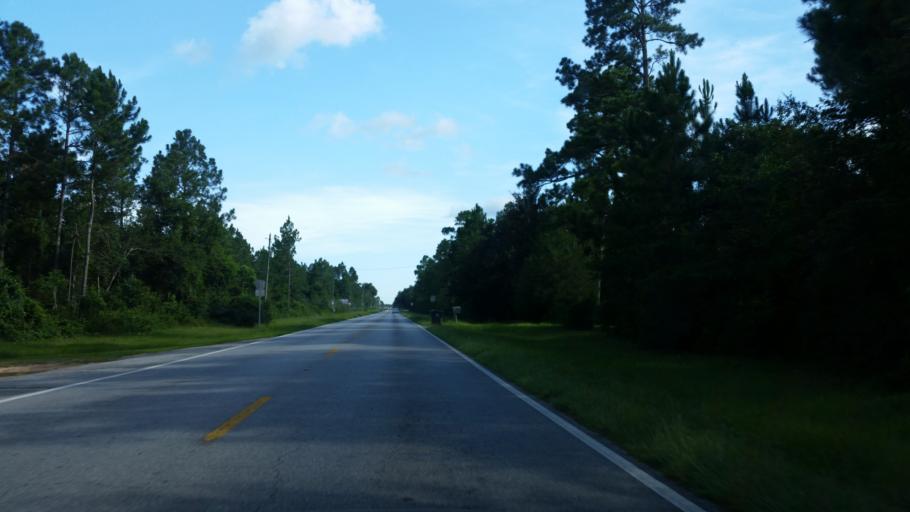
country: US
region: Florida
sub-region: Santa Rosa County
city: Bagdad
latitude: 30.5866
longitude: -87.0311
